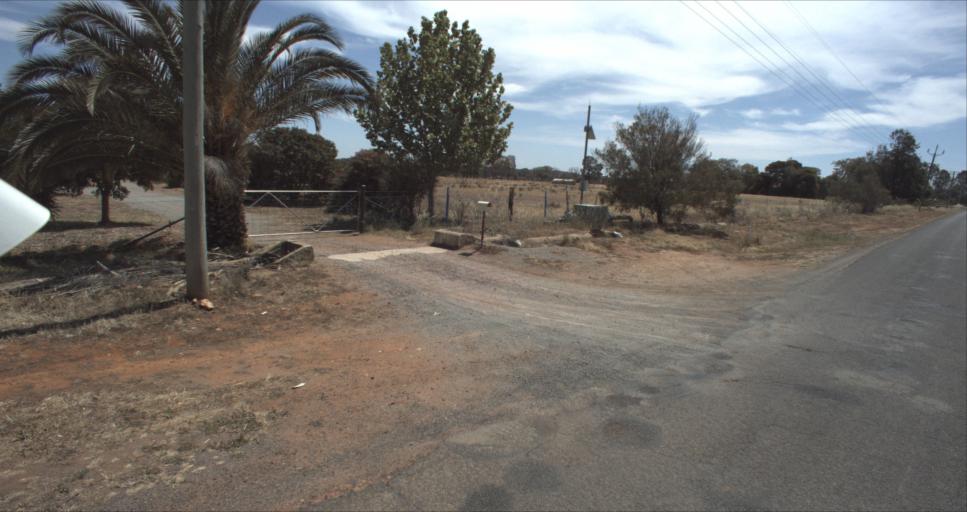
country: AU
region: New South Wales
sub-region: Leeton
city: Leeton
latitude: -34.5962
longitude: 146.4279
